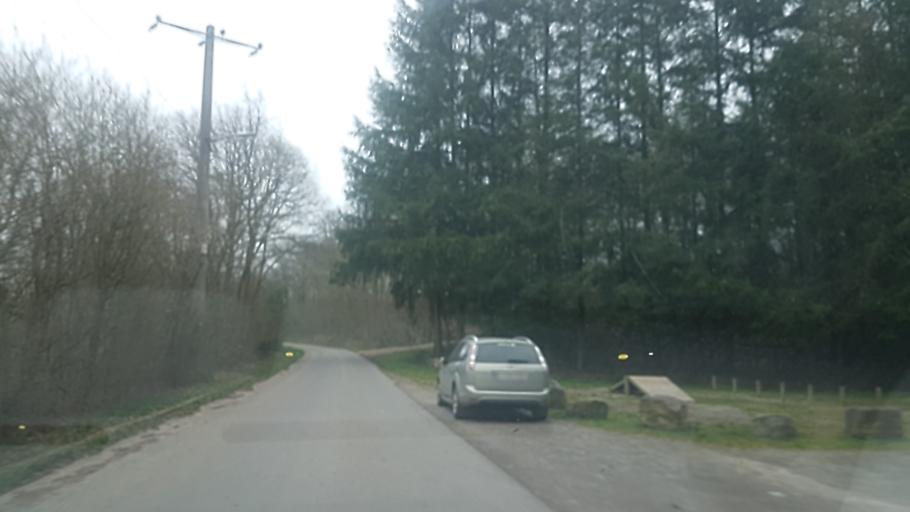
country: FR
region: Champagne-Ardenne
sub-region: Departement des Ardennes
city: Vireux-Molhain
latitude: 50.0780
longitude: 4.6421
